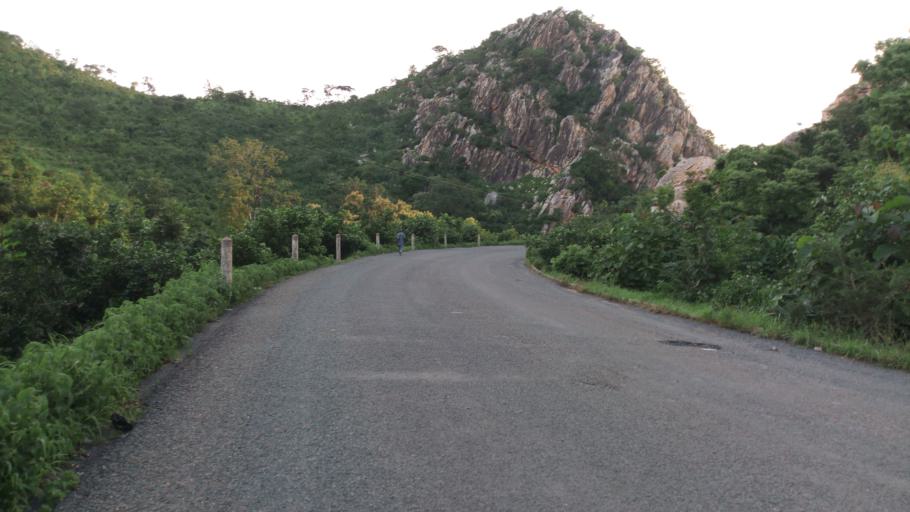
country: BJ
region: Atakora
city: Tanguieta
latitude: 10.6131
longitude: 1.2777
